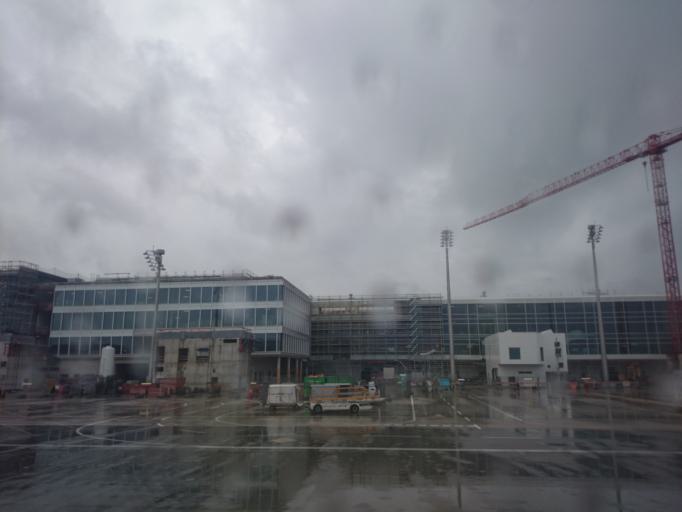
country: DE
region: Bavaria
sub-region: Upper Bavaria
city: Marzling
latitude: 48.3560
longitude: 11.8006
